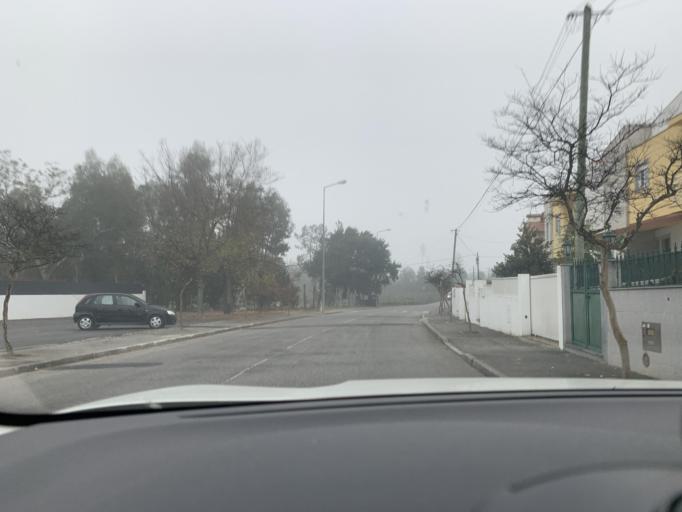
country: PT
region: Viseu
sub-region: Viseu
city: Viseu
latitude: 40.6364
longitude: -7.9186
